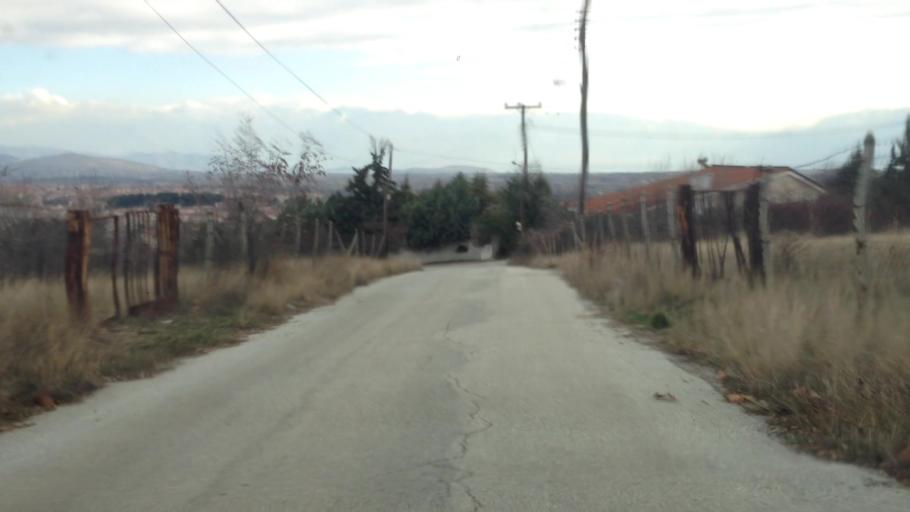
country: GR
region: West Macedonia
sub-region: Nomos Kozanis
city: Kozani
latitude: 40.2923
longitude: 21.7707
